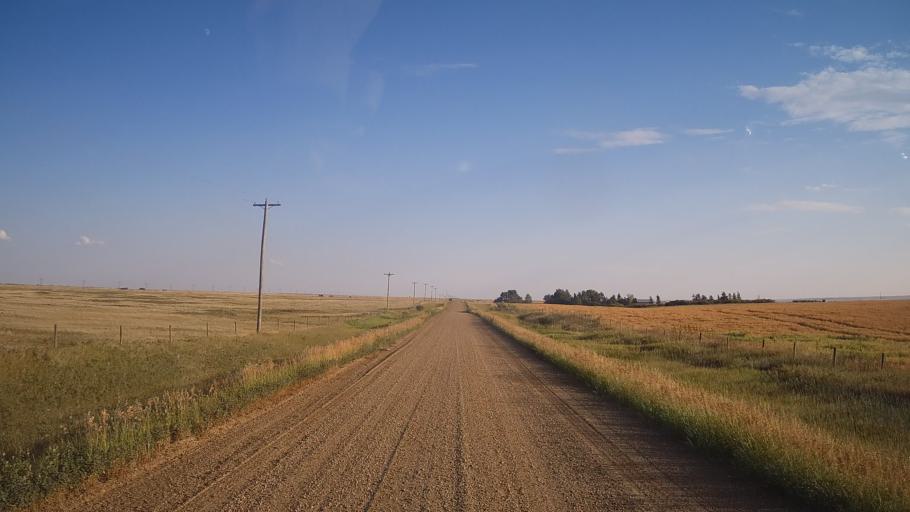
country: CA
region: Alberta
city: Hanna
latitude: 51.6177
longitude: -111.8568
